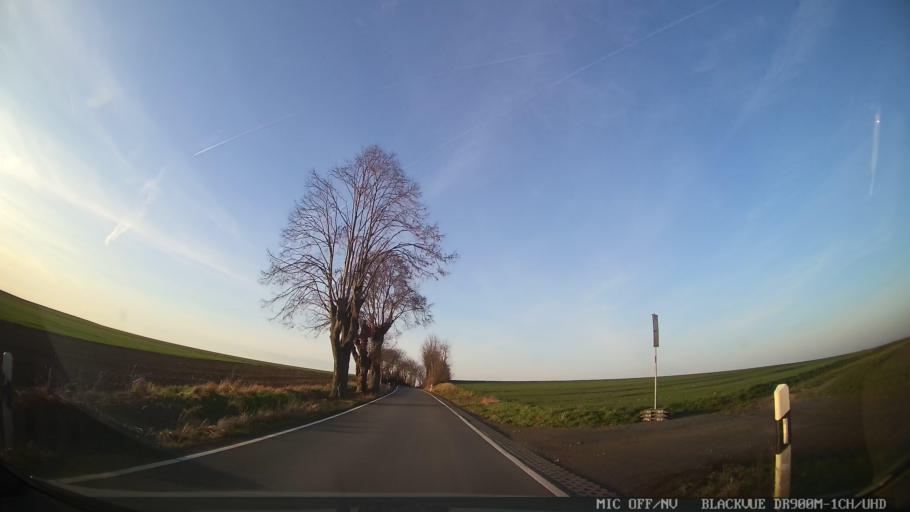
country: DE
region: Hesse
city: Reinheim
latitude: 49.8528
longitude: 8.8777
